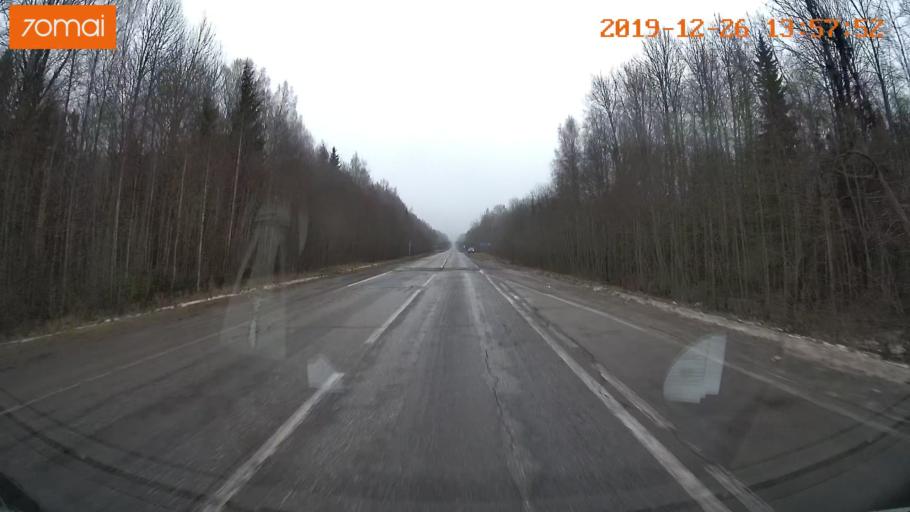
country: RU
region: Jaroslavl
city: Poshekhon'ye
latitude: 58.5787
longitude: 38.6886
